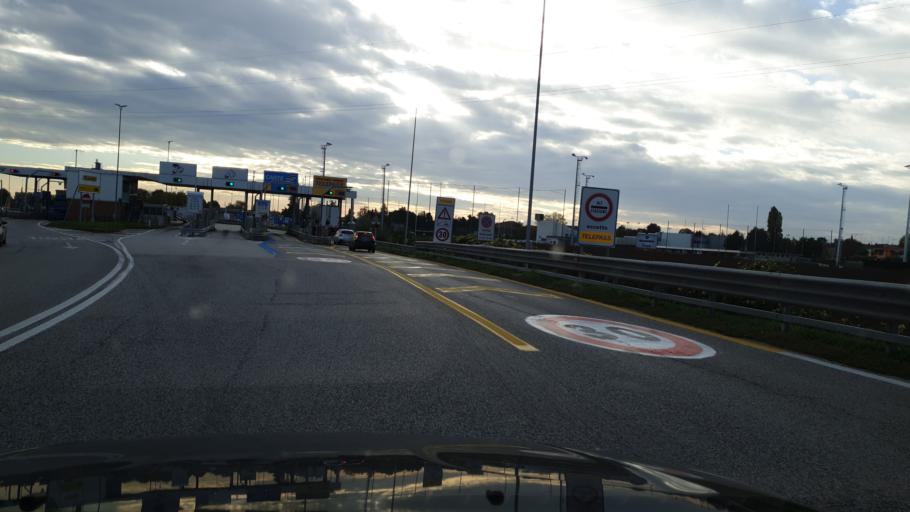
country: IT
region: Veneto
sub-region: Provincia di Padova
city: Monselice
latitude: 45.2393
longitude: 11.7722
